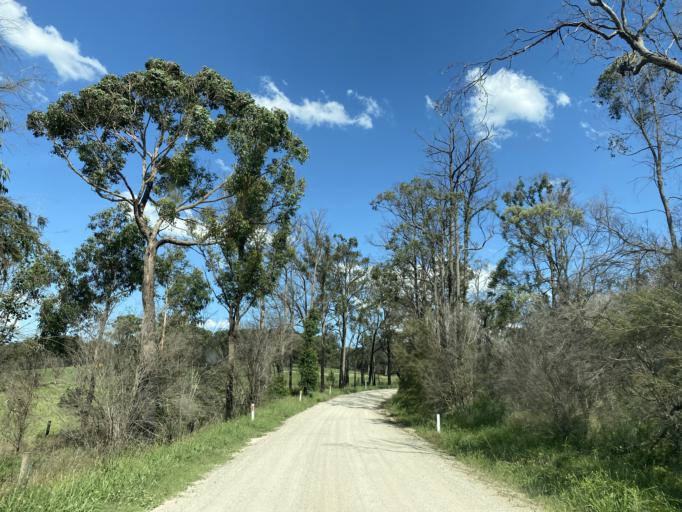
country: AU
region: Victoria
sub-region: Cardinia
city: Bunyip
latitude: -38.0310
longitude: 145.7473
